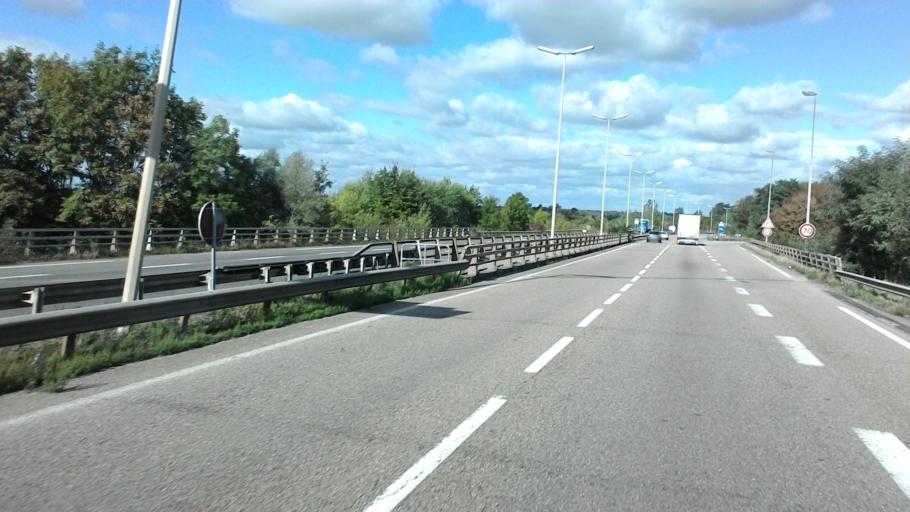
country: FR
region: Lorraine
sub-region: Departement de Meurthe-et-Moselle
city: Dommartin-les-Toul
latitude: 48.6730
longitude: 5.9200
